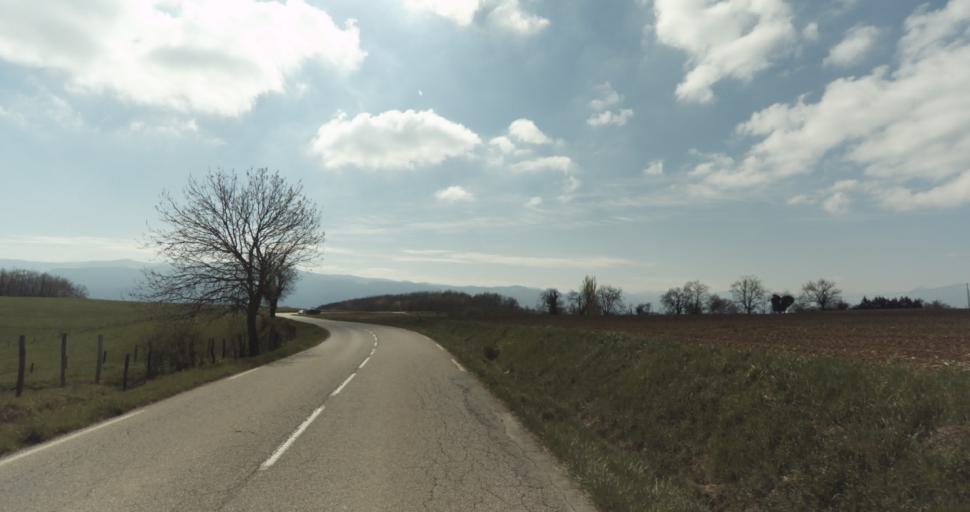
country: FR
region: Rhone-Alpes
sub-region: Departement de l'Isere
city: Saint-Verand
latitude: 45.1825
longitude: 5.3148
